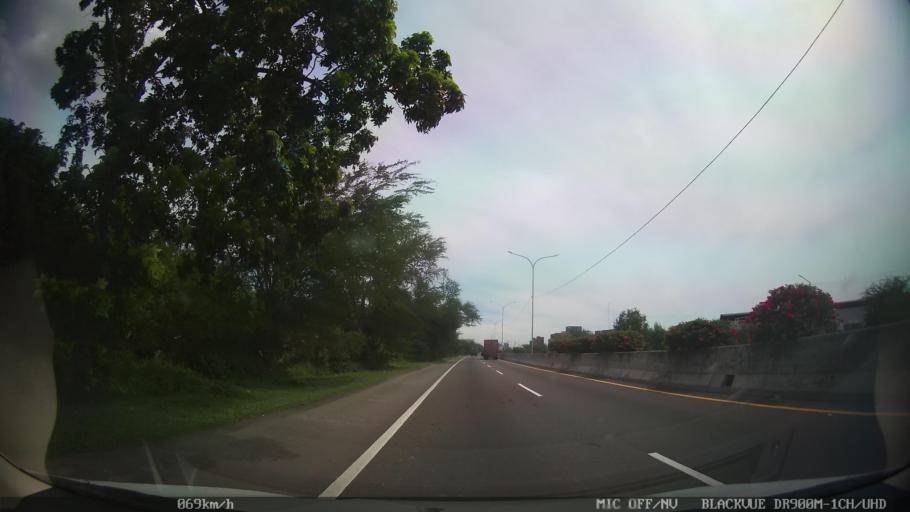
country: ID
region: North Sumatra
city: Belawan
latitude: 3.7649
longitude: 98.6835
